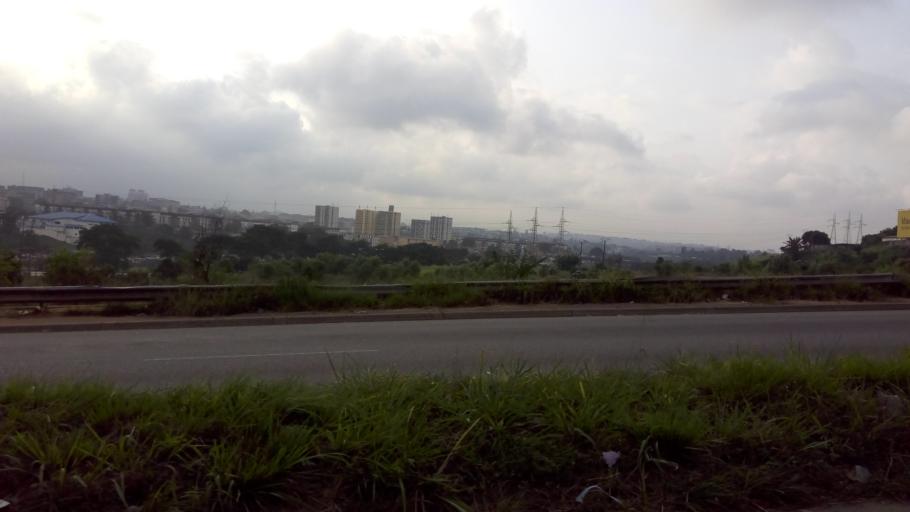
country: CI
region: Lagunes
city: Abidjan
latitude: 5.3466
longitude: -4.0115
